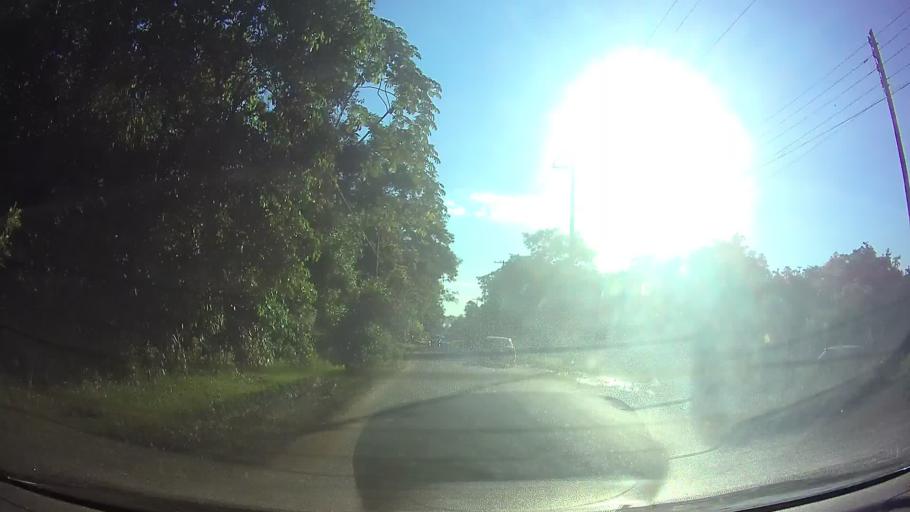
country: PY
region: Cordillera
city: San Bernardino
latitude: -25.3240
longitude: -57.2781
